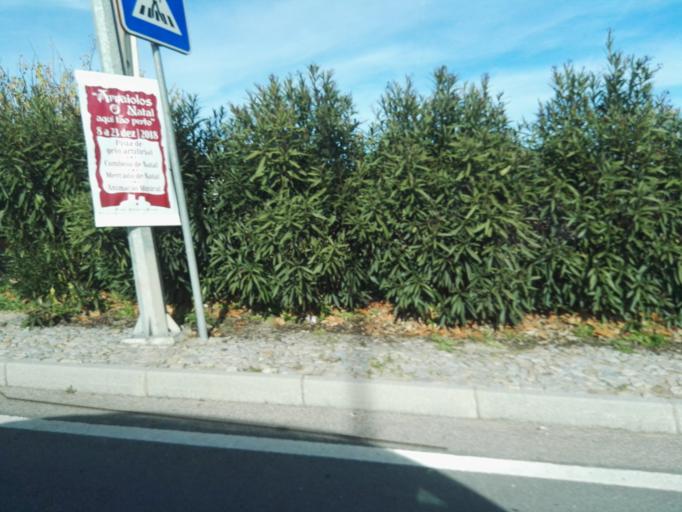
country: PT
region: Evora
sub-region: Mora
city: Mora
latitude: 38.8928
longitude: -8.0173
